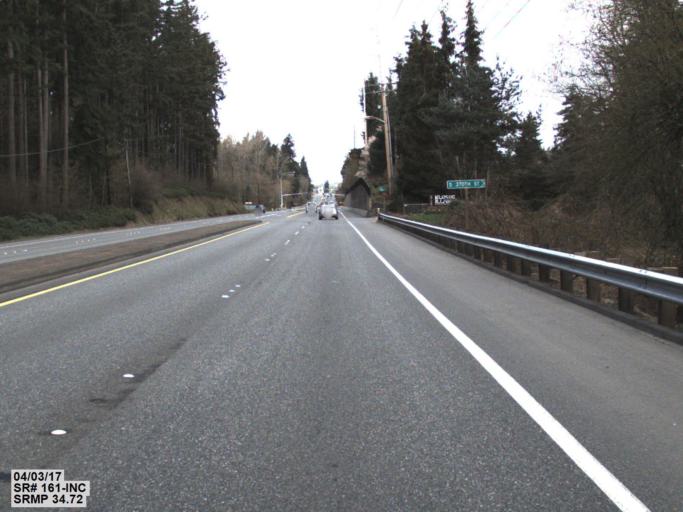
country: US
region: Washington
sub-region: Pierce County
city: Edgewood
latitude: 47.2689
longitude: -122.3030
